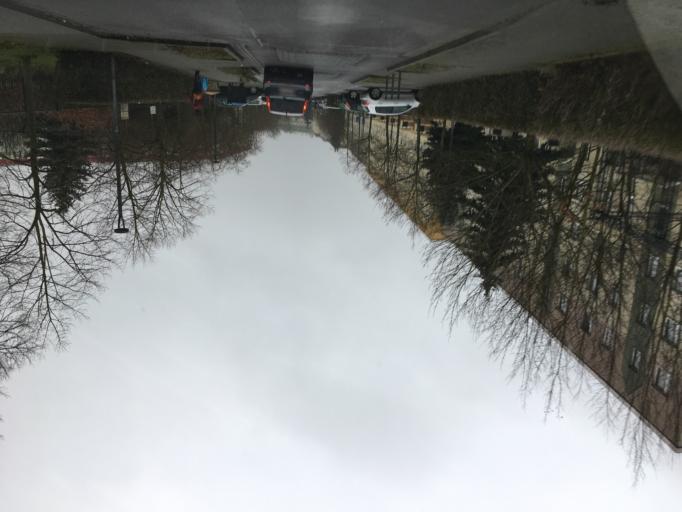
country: DE
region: Saxony-Anhalt
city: Haldensleben I
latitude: 52.2801
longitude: 11.3951
